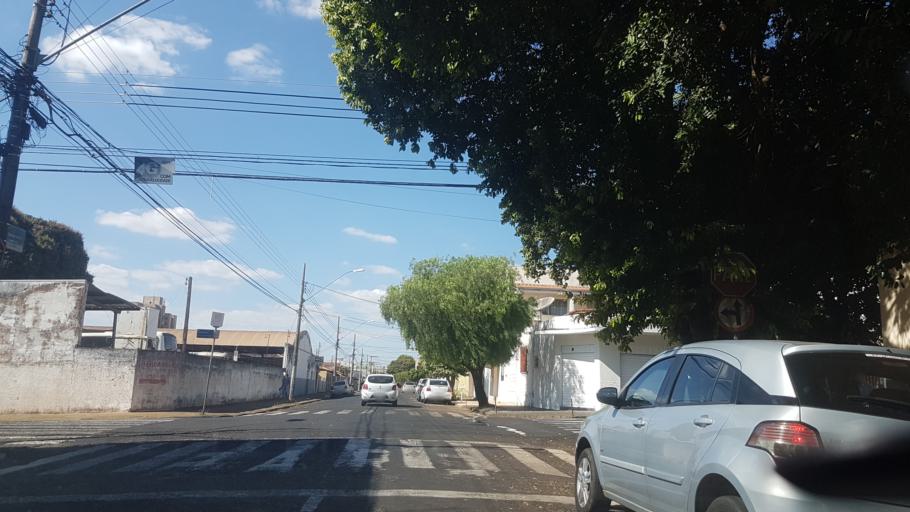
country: BR
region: Minas Gerais
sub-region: Uberlandia
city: Uberlandia
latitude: -18.9086
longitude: -48.2846
